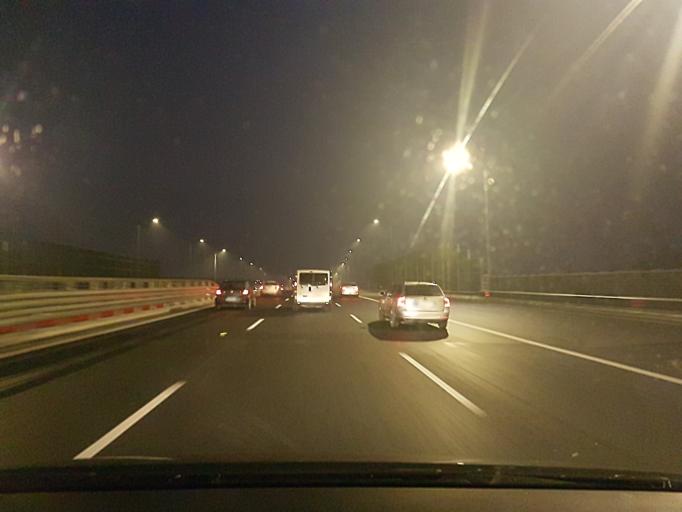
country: PL
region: Masovian Voivodeship
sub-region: Powiat wolominski
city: Marki
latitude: 52.3145
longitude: 21.1292
